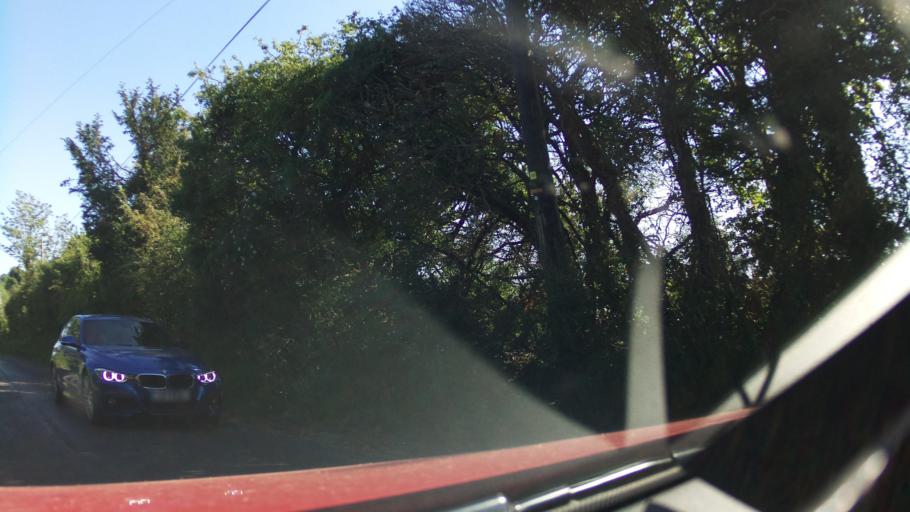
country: GB
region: England
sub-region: Hampshire
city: Winchester
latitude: 51.0842
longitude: -1.3465
